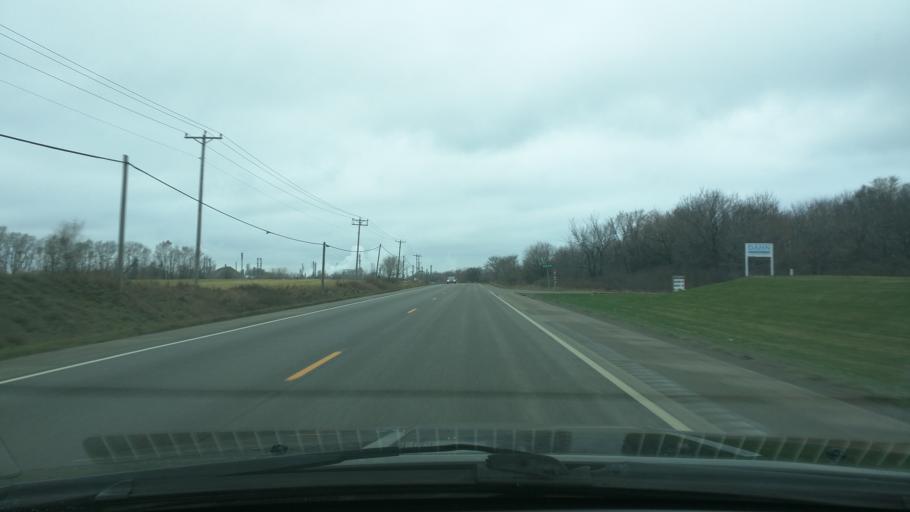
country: US
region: Minnesota
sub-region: Washington County
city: Saint Paul Park
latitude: 44.7577
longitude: -93.0152
